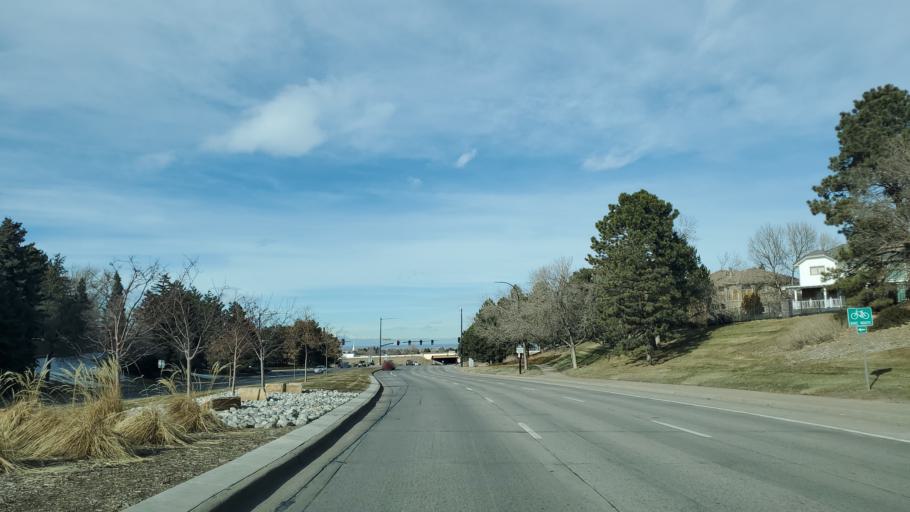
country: US
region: Colorado
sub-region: Douglas County
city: Highlands Ranch
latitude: 39.5593
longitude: -104.9588
